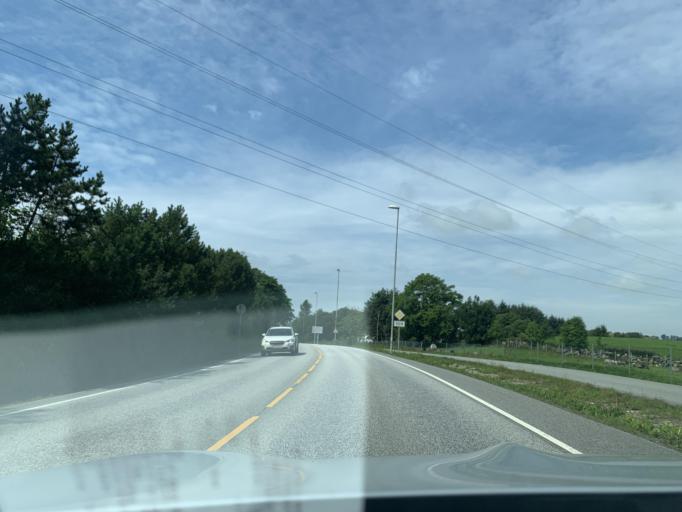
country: NO
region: Rogaland
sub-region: Sandnes
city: Sandnes
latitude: 58.8612
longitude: 5.7047
